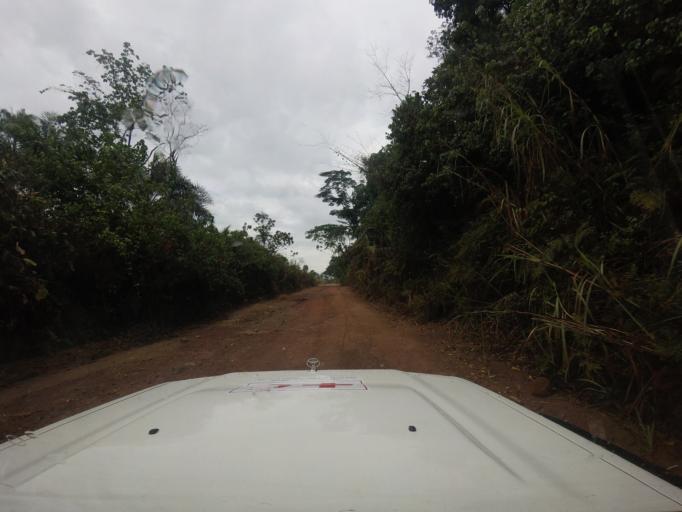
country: SL
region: Eastern Province
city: Buedu
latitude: 8.3441
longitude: -10.1749
